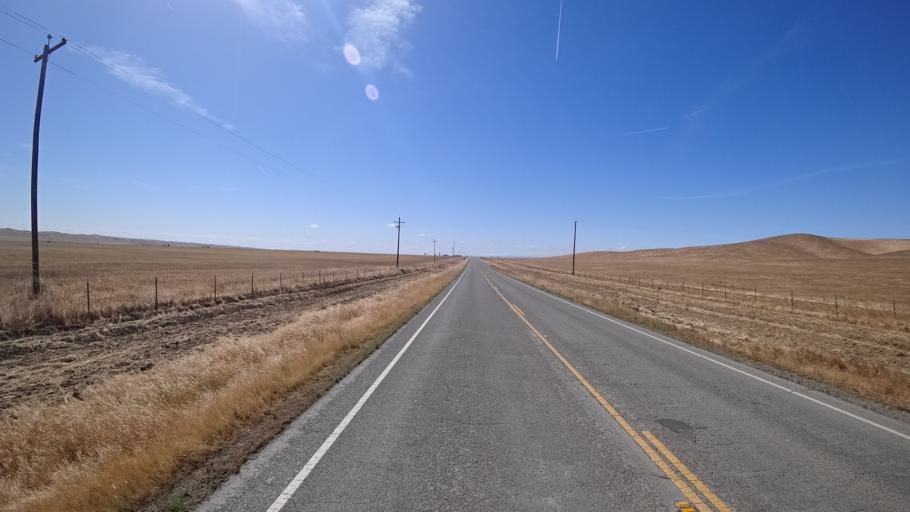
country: US
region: California
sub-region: Kings County
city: Avenal
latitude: 35.9009
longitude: -120.0527
